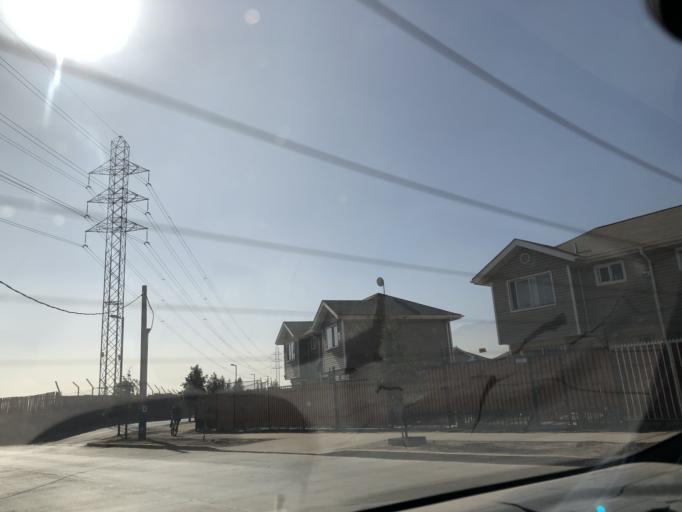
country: CL
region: Santiago Metropolitan
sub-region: Provincia de Cordillera
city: Puente Alto
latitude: -33.5940
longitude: -70.6003
